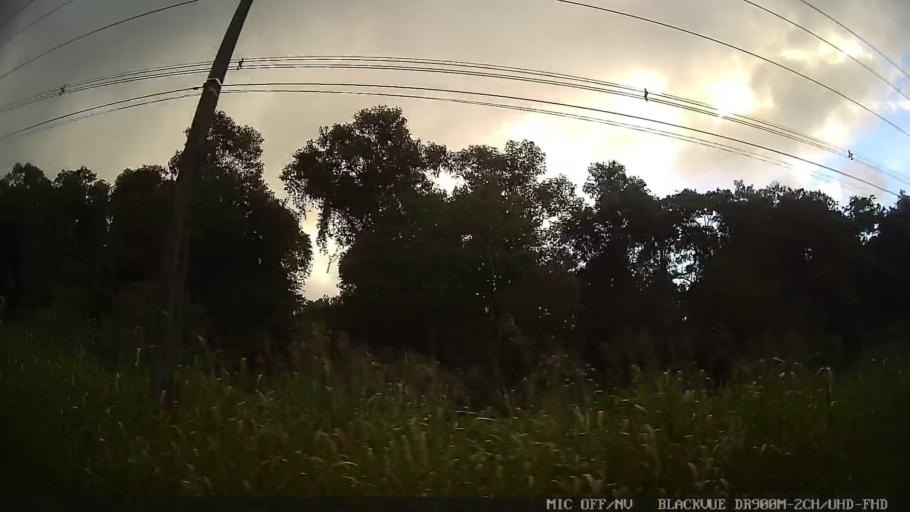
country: BR
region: Sao Paulo
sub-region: Itanhaem
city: Itanhaem
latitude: -24.1131
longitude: -46.7965
